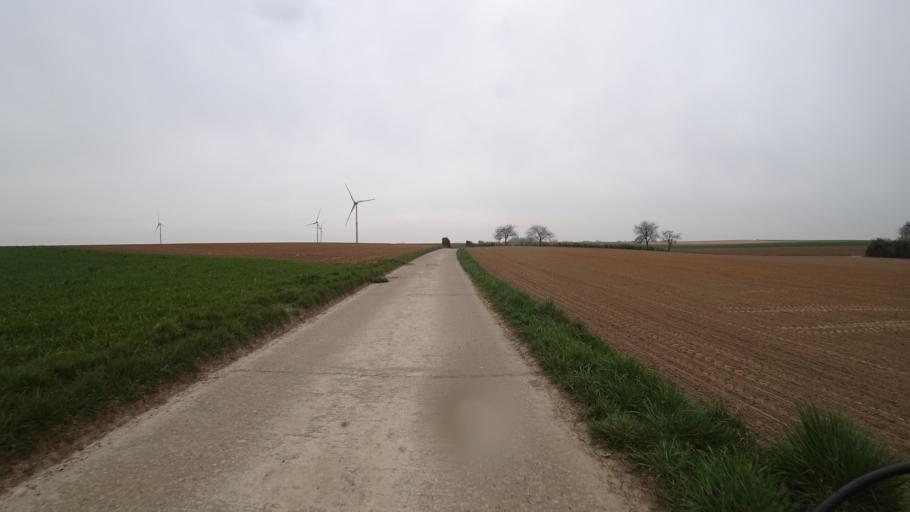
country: BE
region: Wallonia
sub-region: Province du Brabant Wallon
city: Walhain-Saint-Paul
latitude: 50.6075
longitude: 4.6927
